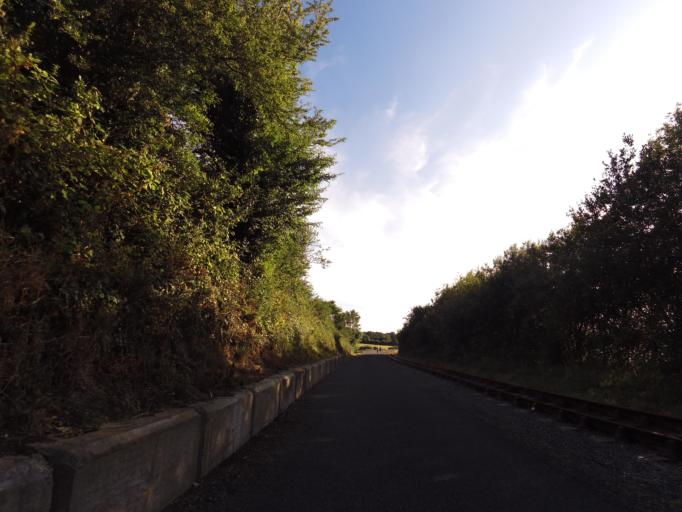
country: IE
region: Leinster
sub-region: Kilkenny
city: Mooncoin
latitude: 52.2484
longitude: -7.1969
